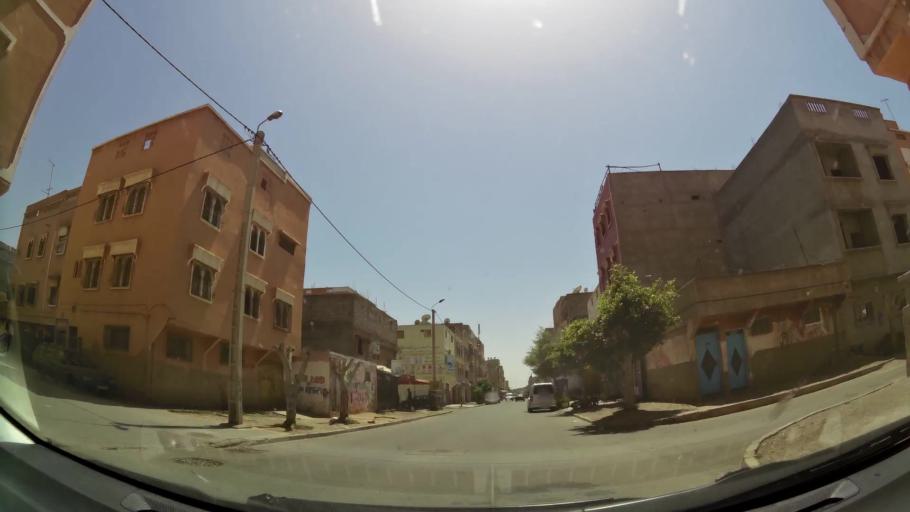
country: MA
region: Souss-Massa-Draa
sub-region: Inezgane-Ait Mellou
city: Inezgane
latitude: 30.3494
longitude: -9.4897
